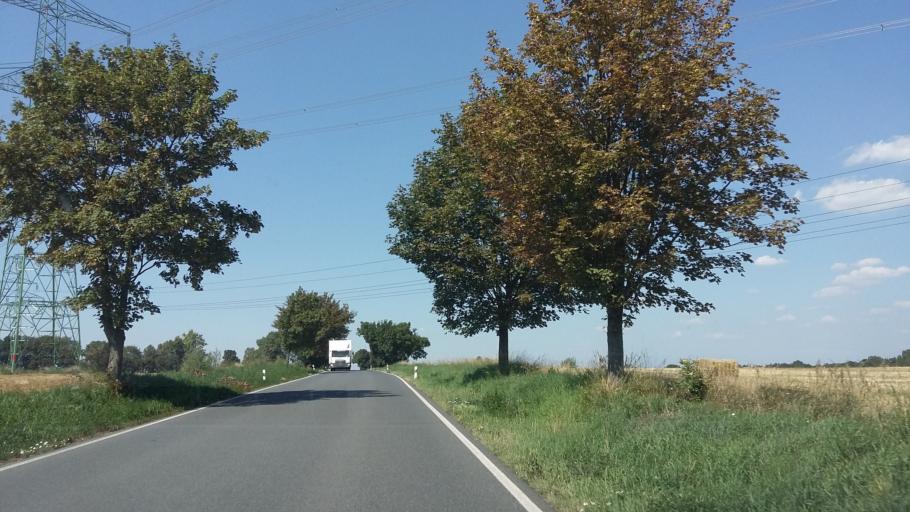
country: CZ
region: Central Bohemia
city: Zelenec
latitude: 50.1521
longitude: 14.6873
